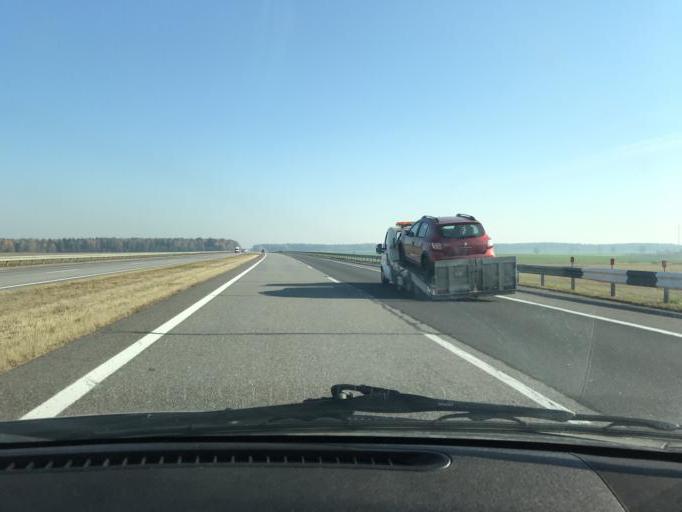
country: BY
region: Vitebsk
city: Talachyn
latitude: 54.4641
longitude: 29.7482
